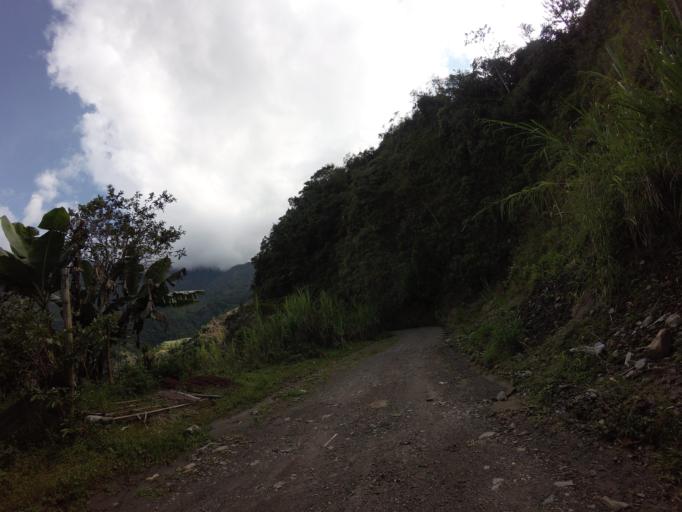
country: CO
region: Caldas
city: Pensilvania
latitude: 5.4594
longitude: -75.1617
